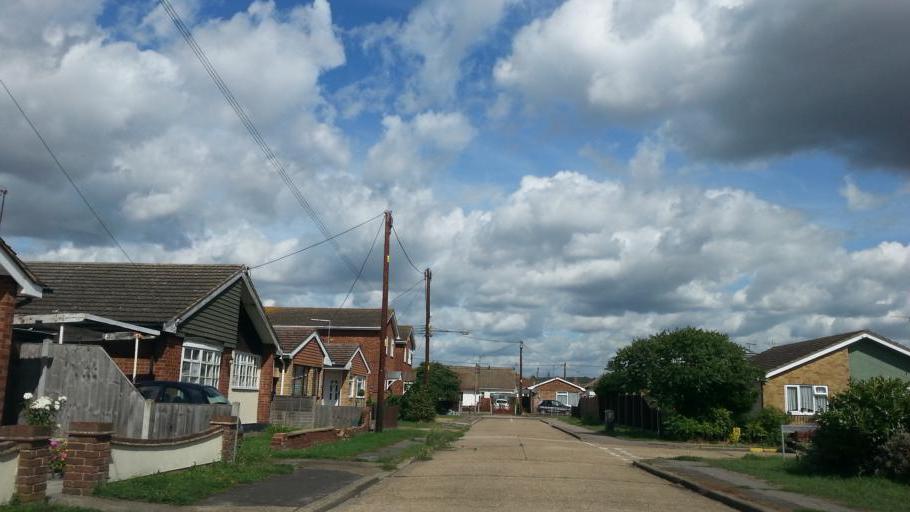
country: GB
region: England
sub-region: Essex
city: Canvey Island
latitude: 51.5233
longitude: 0.5834
